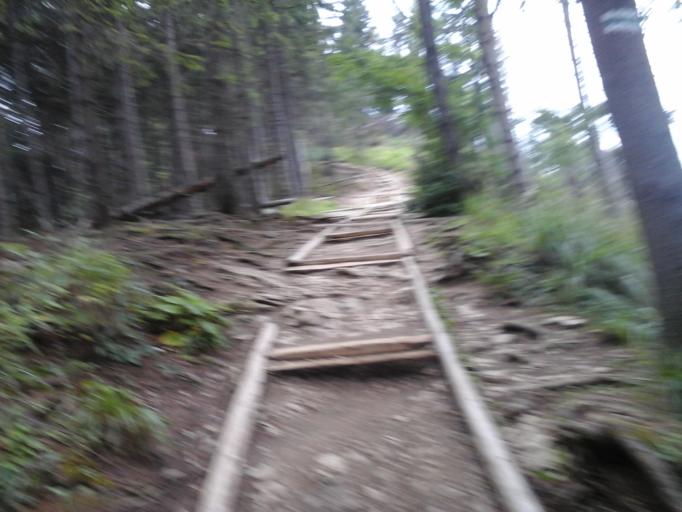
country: PL
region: Lesser Poland Voivodeship
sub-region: Powiat tatrzanski
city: Zakopane
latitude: 49.2733
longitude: 19.9914
